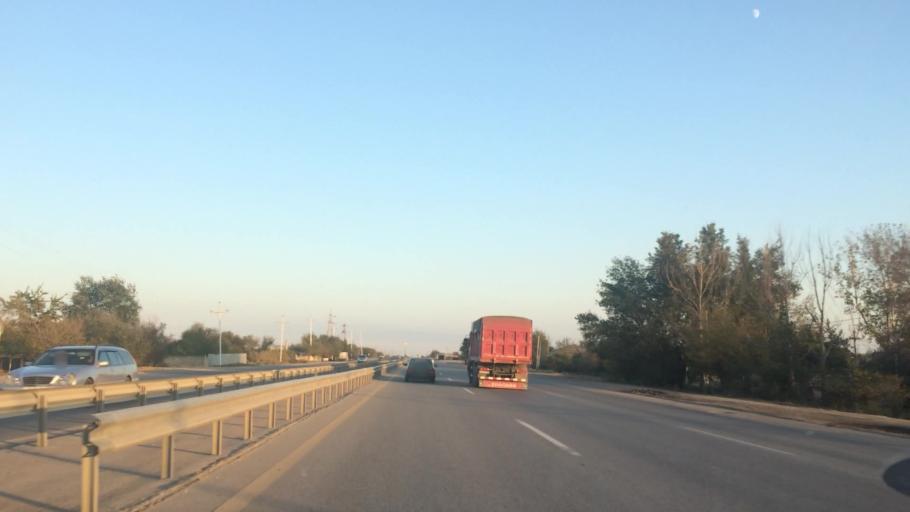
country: AZ
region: Haciqabul
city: Haciqabul
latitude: 40.0152
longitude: 49.1381
